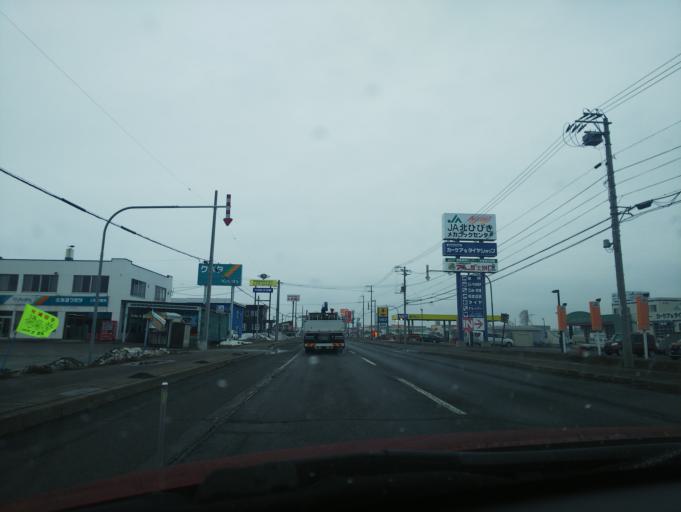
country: JP
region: Hokkaido
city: Nayoro
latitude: 44.1601
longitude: 142.3972
